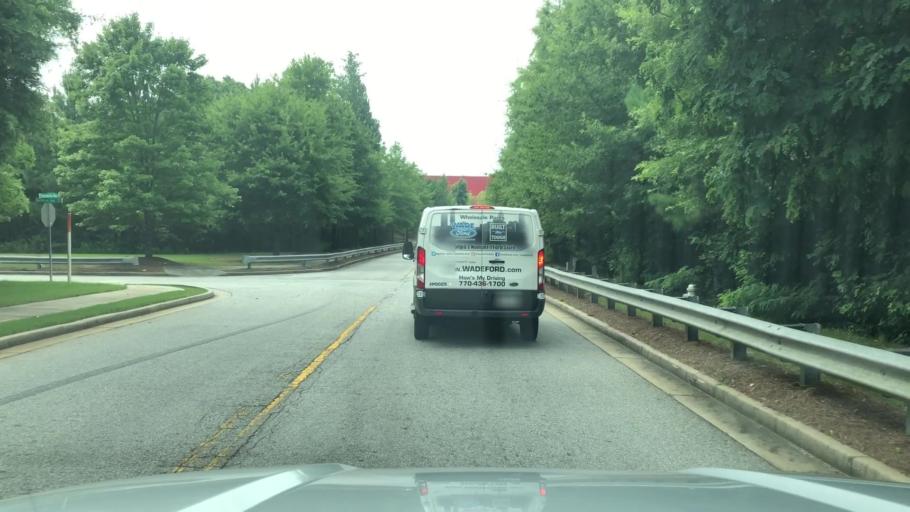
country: US
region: Georgia
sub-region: Cobb County
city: Mableton
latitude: 33.7698
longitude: -84.5766
